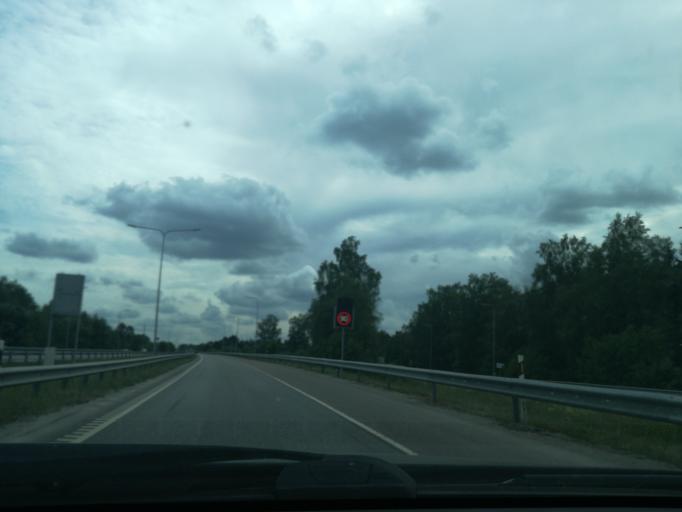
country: EE
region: Harju
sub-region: Saue linn
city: Saue
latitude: 59.2479
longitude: 24.4959
